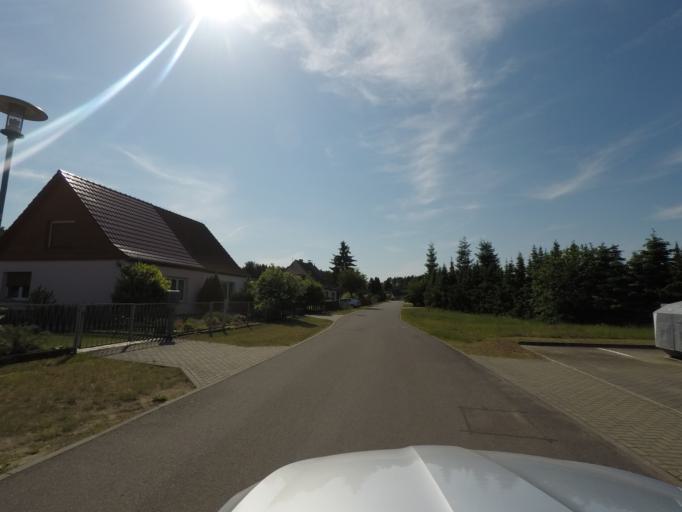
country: DE
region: Brandenburg
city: Melchow
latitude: 52.8610
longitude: 13.7200
